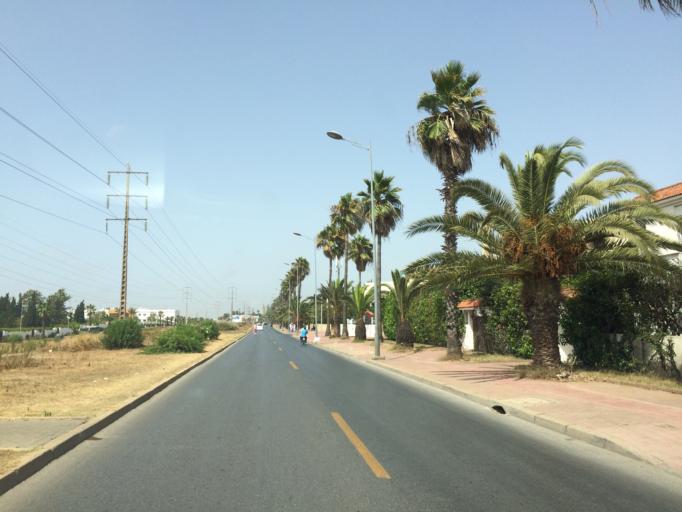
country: MA
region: Rabat-Sale-Zemmour-Zaer
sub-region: Skhirate-Temara
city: Temara
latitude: 33.9659
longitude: -6.8696
